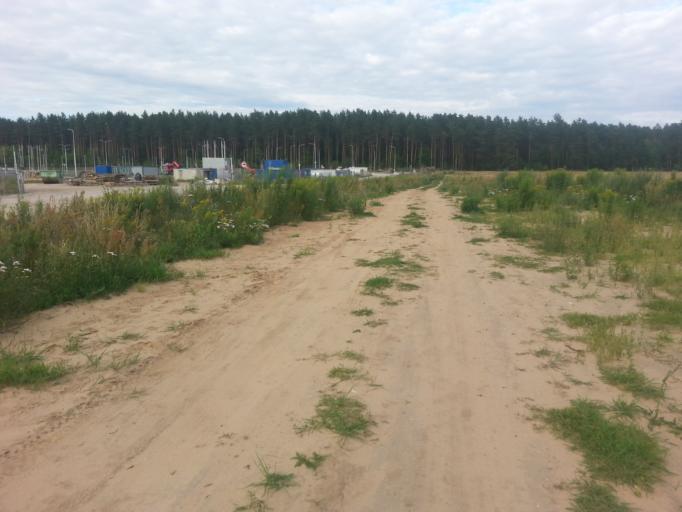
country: LV
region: Stopini
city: Ulbroka
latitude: 56.9515
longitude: 24.2545
